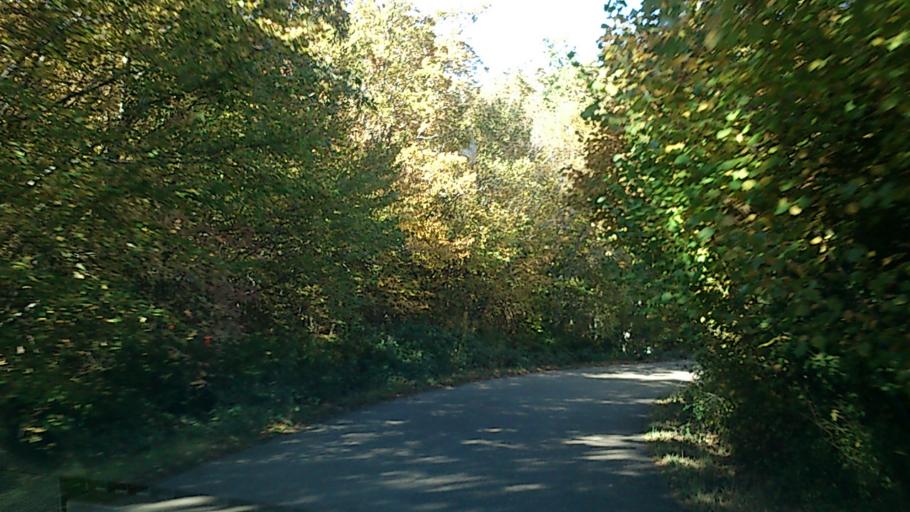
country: ES
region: Aragon
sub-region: Provincia de Zaragoza
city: Litago
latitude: 41.7988
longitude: -1.7894
